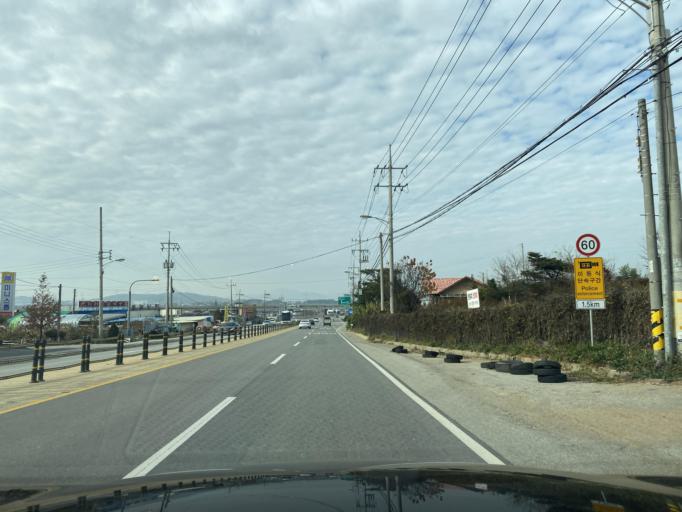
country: KR
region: Chungcheongnam-do
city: Yesan
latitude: 36.6861
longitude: 126.7764
